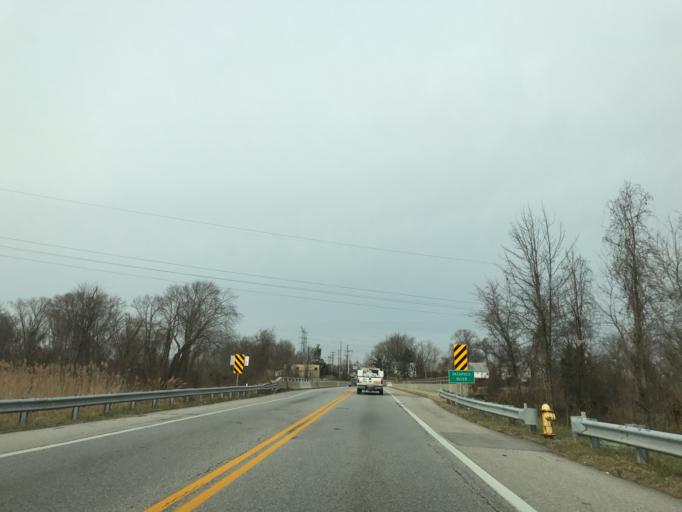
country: US
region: Maryland
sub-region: Anne Arundel County
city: Pumphrey
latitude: 39.2244
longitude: -76.6416
